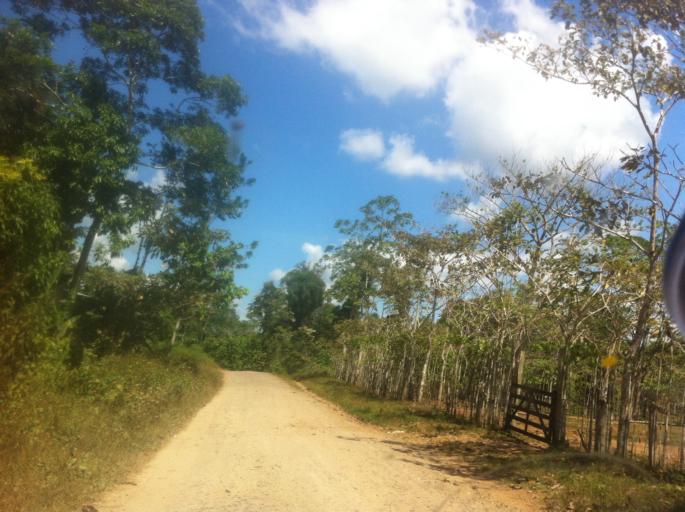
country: CR
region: Alajuela
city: Los Chiles
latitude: 11.2329
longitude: -84.5013
